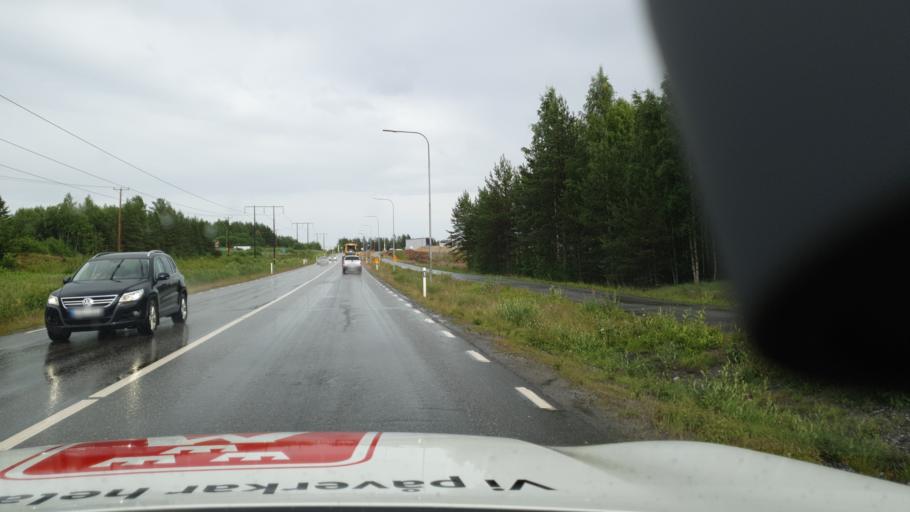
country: SE
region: Vaesterbotten
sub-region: Umea Kommun
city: Roback
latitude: 63.8495
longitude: 20.1461
